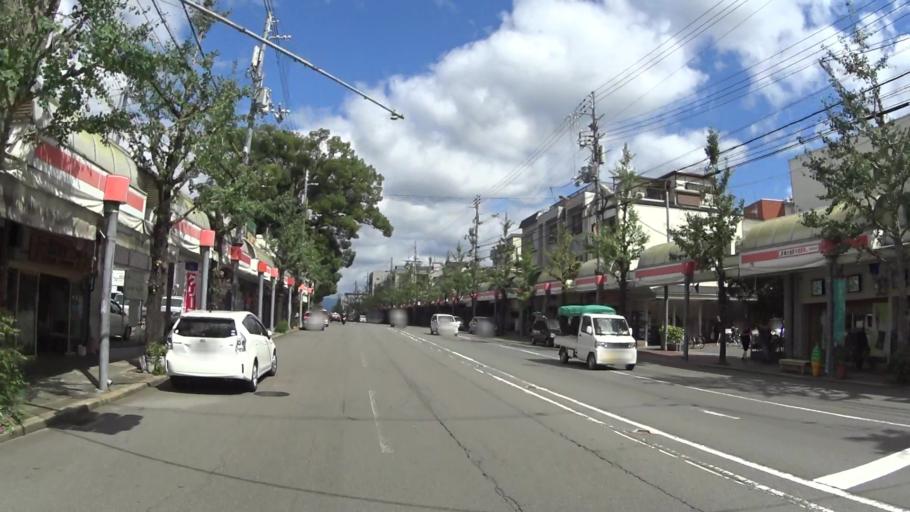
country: JP
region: Kyoto
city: Kyoto
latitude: 34.9836
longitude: 135.7739
